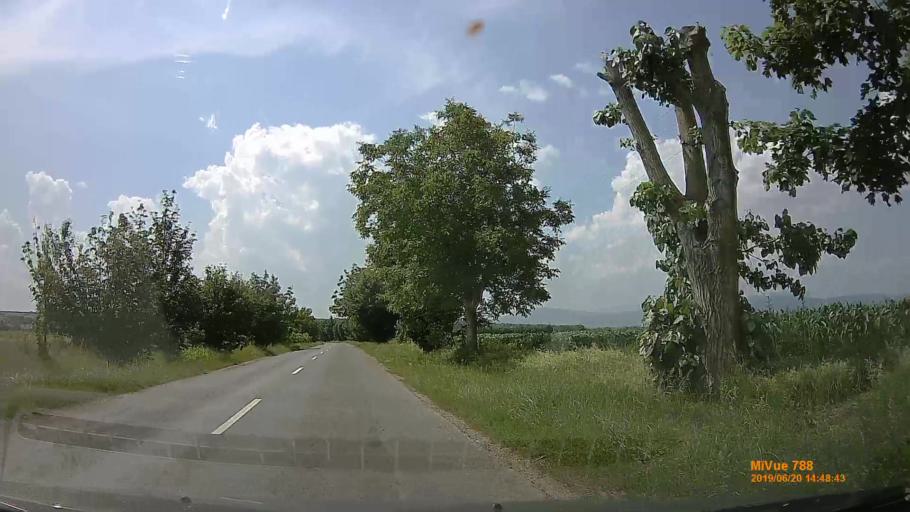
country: HU
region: Baranya
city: Kozarmisleny
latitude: 46.0157
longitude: 18.2844
